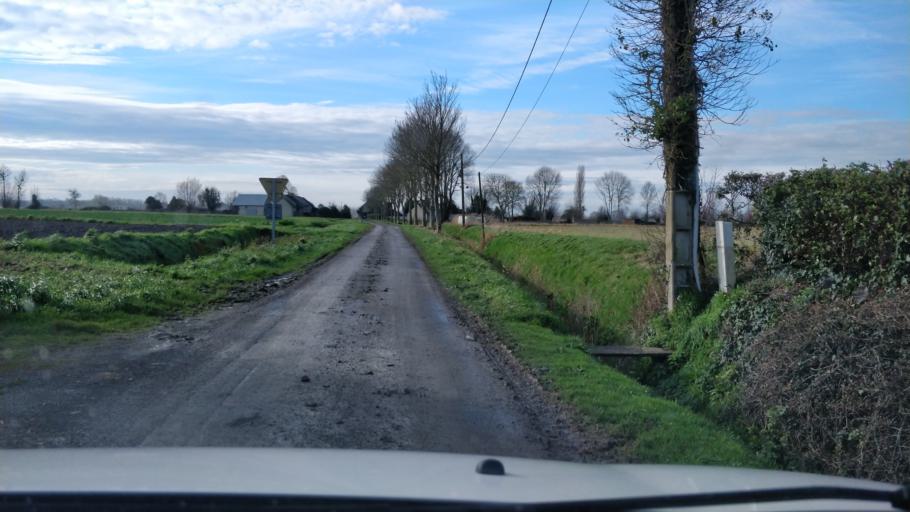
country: FR
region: Brittany
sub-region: Departement d'Ille-et-Vilaine
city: La Fresnais
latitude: 48.5783
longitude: -1.8176
